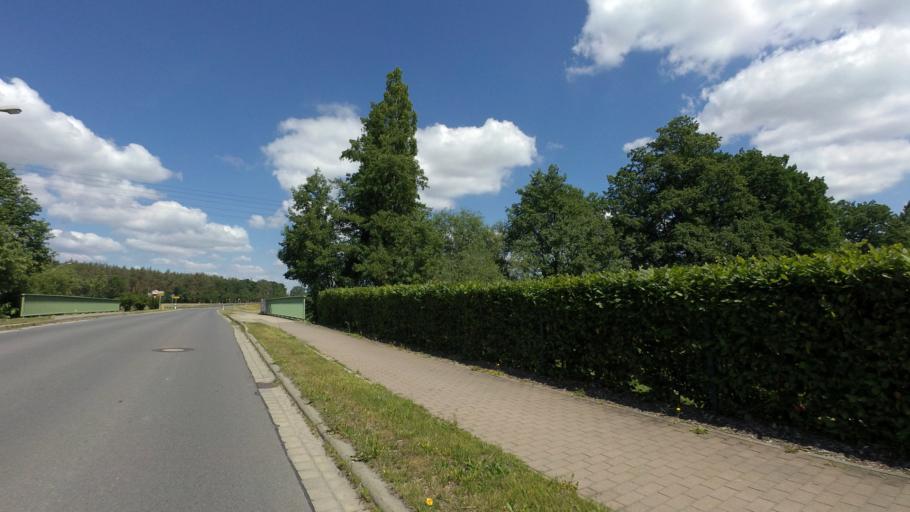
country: DE
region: Brandenburg
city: Sonnewalde
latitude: 51.6693
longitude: 13.6426
